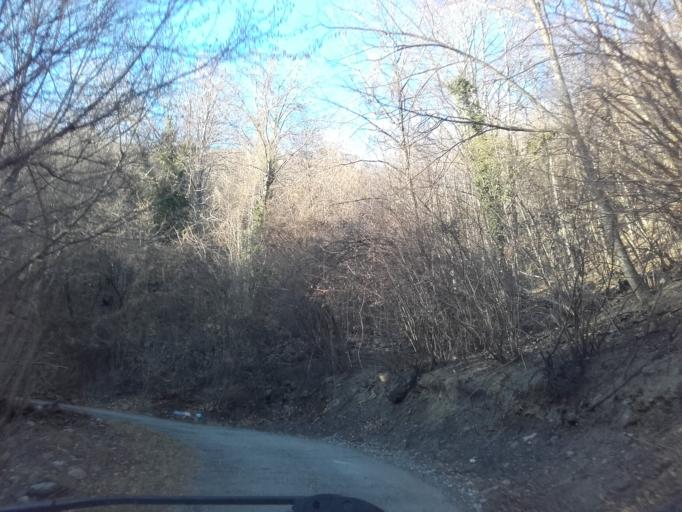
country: IT
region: Piedmont
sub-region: Provincia di Torino
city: Bussoleno
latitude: 45.1534
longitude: 7.1383
